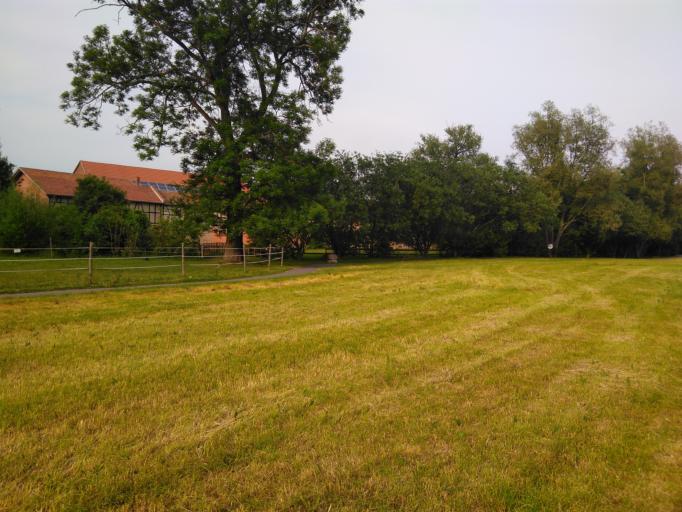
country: DE
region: Thuringia
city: Kromsdorf
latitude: 51.0021
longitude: 11.3647
